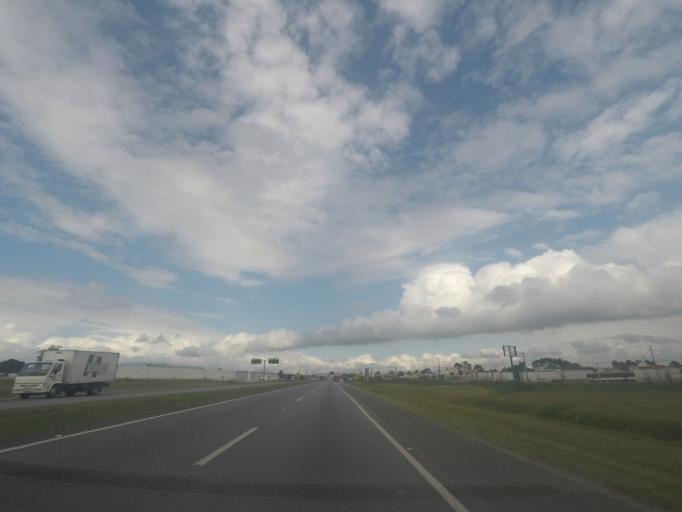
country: BR
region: Parana
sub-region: Sao Jose Dos Pinhais
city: Sao Jose dos Pinhais
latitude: -25.5124
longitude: -49.1263
